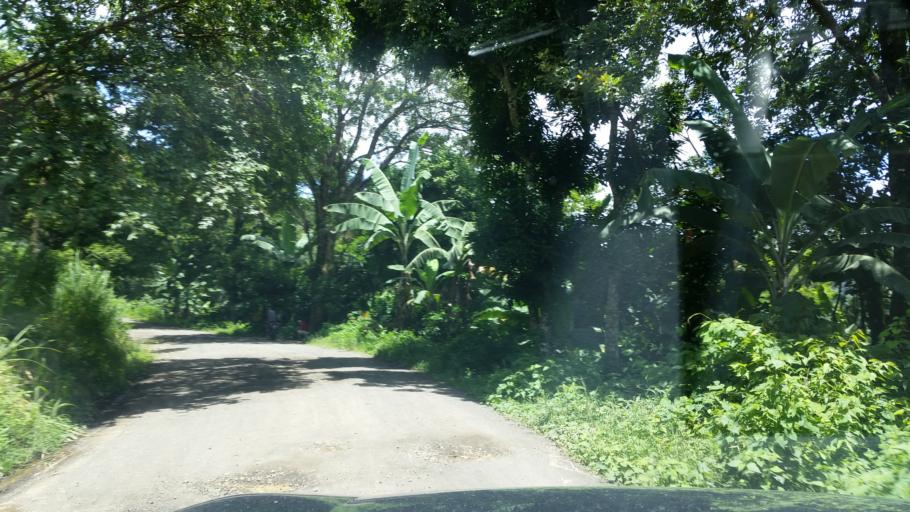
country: NI
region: Atlantico Norte (RAAN)
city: Waslala
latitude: 13.2506
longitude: -85.6145
